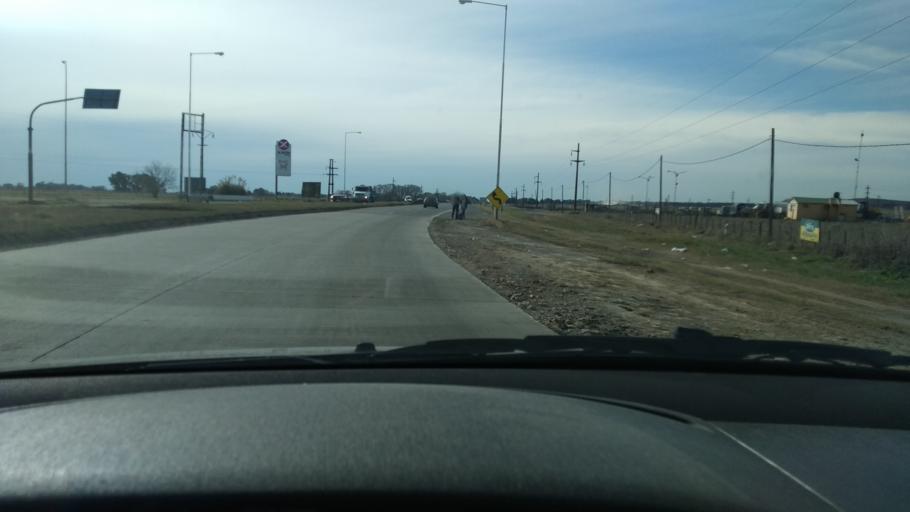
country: AR
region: Buenos Aires
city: Olavarria
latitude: -36.9359
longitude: -60.2288
